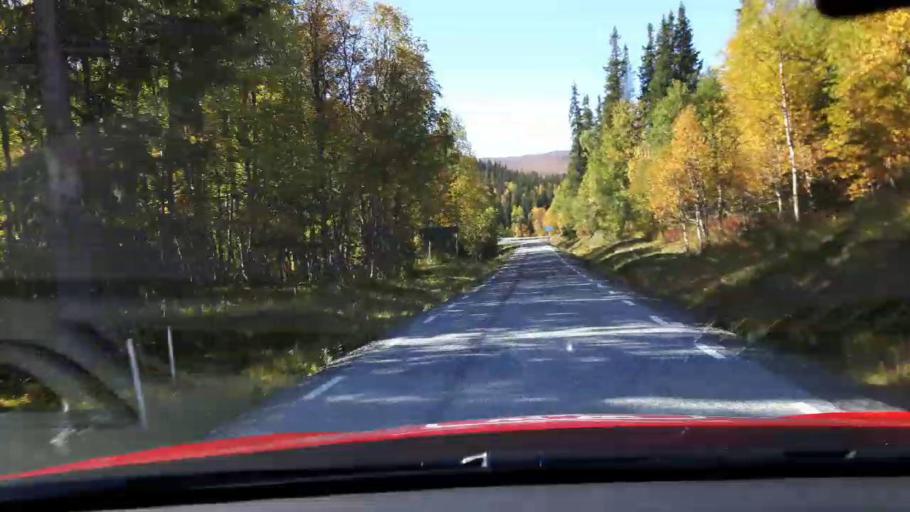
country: NO
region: Nord-Trondelag
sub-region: Royrvik
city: Royrvik
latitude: 64.8776
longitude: 14.2188
